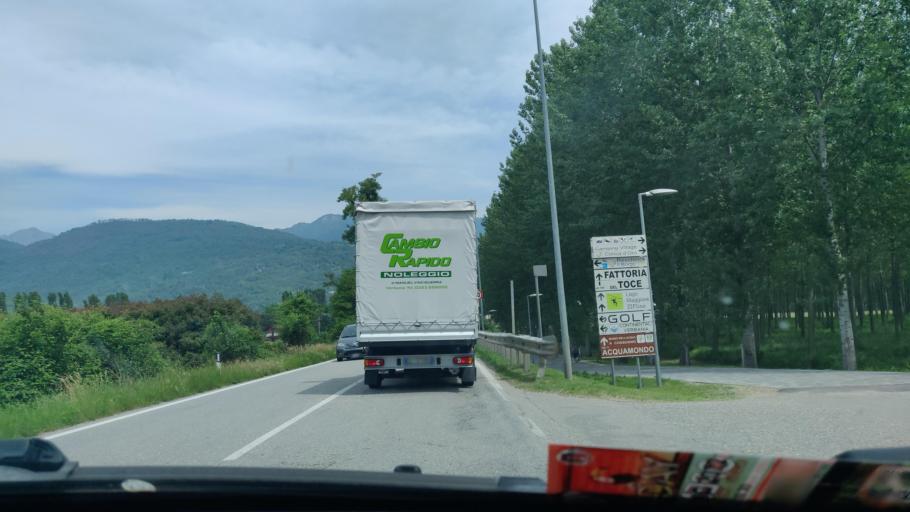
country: IT
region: Piedmont
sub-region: Provincia Verbano-Cusio-Ossola
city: Baveno
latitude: 45.9355
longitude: 8.4823
